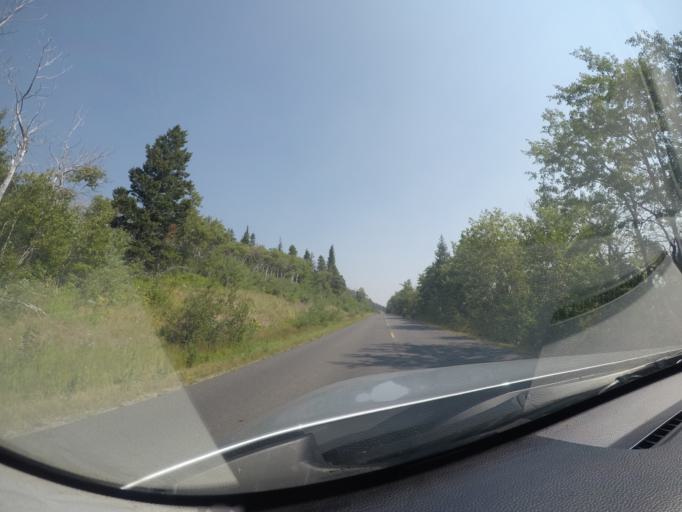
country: US
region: Montana
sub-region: Glacier County
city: Browning
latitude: 48.7008
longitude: -113.5039
